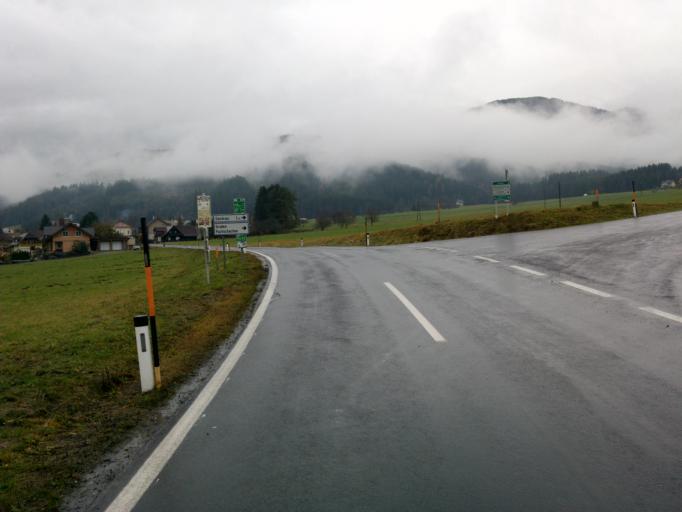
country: AT
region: Styria
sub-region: Politischer Bezirk Murtal
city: Gaal
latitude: 47.2701
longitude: 14.7151
